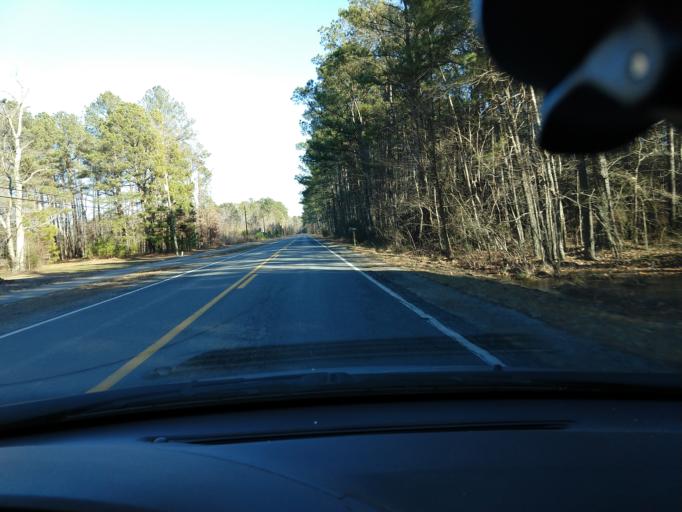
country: US
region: Virginia
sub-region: Charles City County
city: Charles City
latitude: 37.3259
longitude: -76.9949
